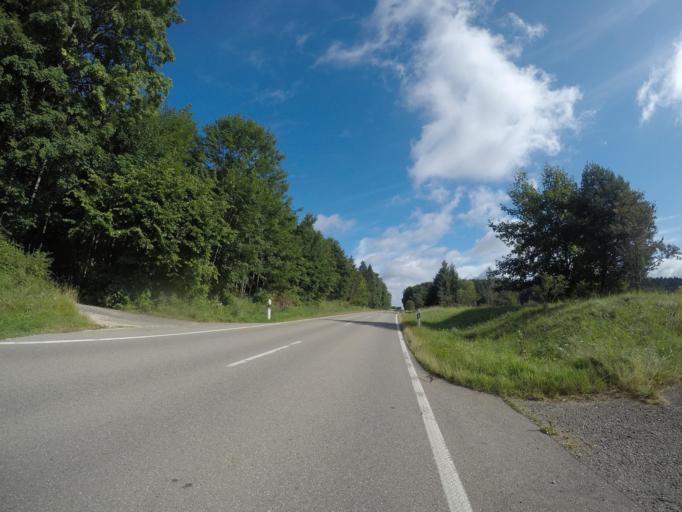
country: DE
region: Baden-Wuerttemberg
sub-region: Tuebingen Region
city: Laichingen
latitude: 48.4141
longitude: 9.6498
